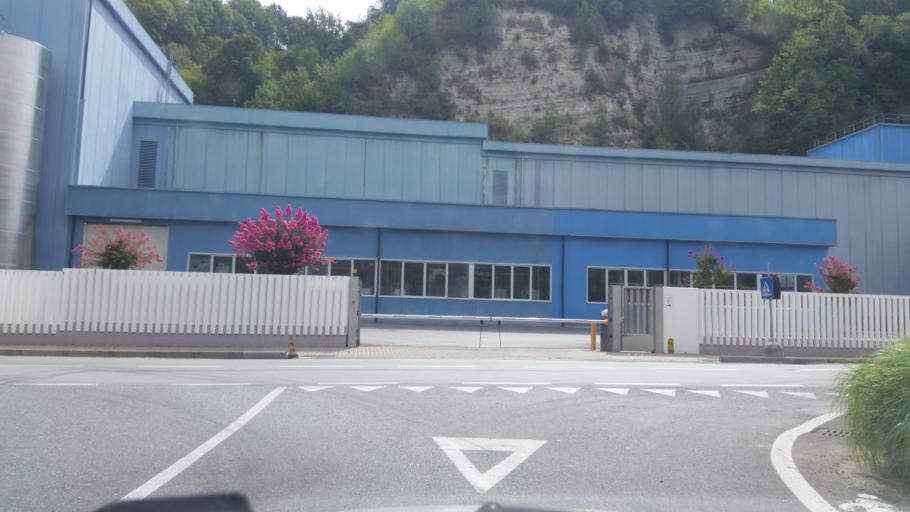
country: IT
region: Piedmont
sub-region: Provincia di Cuneo
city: Cossano Belbo
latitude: 44.6823
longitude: 8.2019
